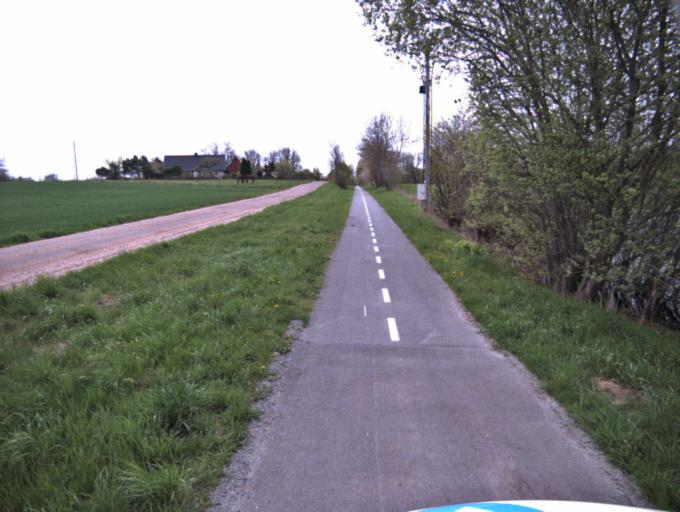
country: SE
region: Skane
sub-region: Kristianstads Kommun
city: Onnestad
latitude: 55.9924
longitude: 14.0348
